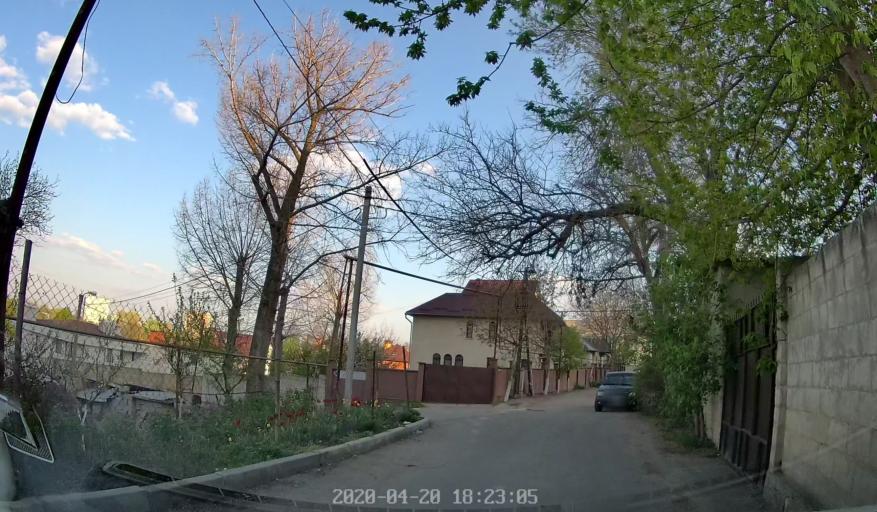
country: MD
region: Chisinau
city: Chisinau
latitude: 46.9962
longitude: 28.8375
